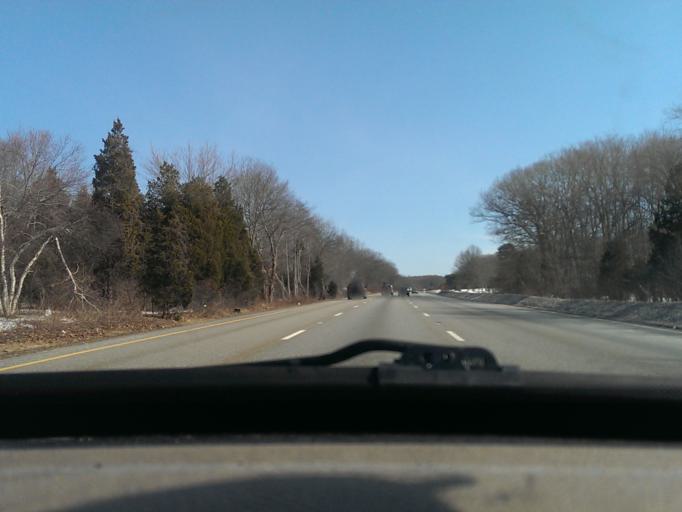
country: US
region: Massachusetts
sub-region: Bristol County
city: Ocean Grove
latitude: 41.7663
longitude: -71.2388
